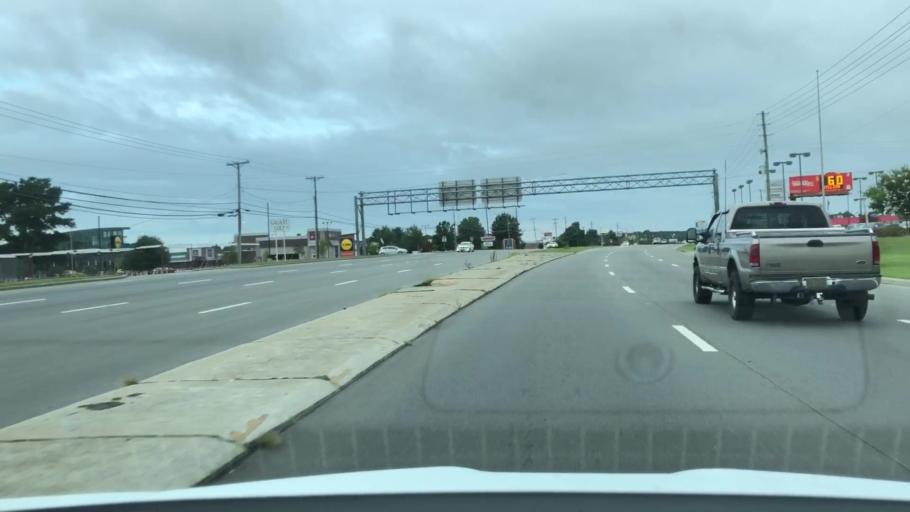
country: US
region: North Carolina
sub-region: Lenoir County
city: Kinston
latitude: 35.2628
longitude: -77.6428
